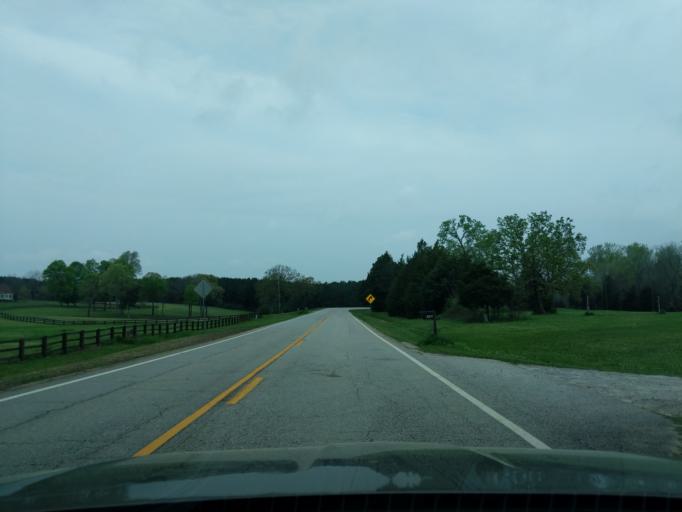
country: US
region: Georgia
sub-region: Lincoln County
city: Lincolnton
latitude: 33.7920
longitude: -82.3820
